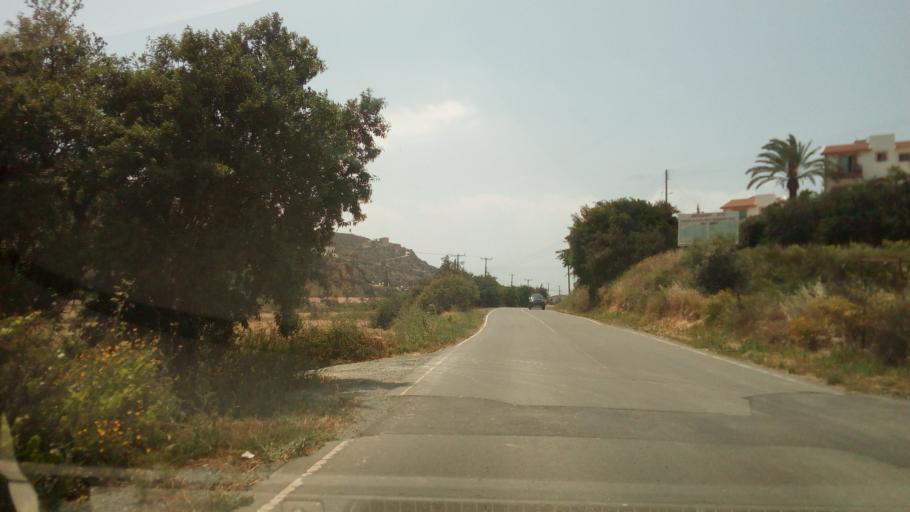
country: CY
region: Limassol
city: Pissouri
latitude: 34.6597
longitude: 32.7284
